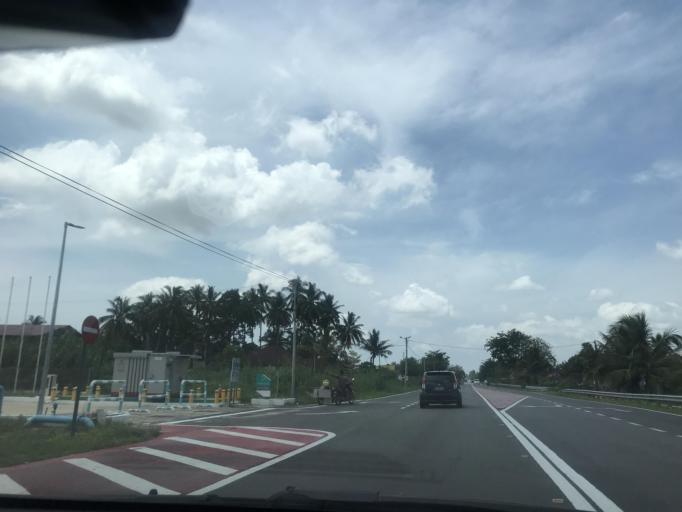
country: MY
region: Kelantan
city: Kota Bharu
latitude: 6.1521
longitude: 102.2077
